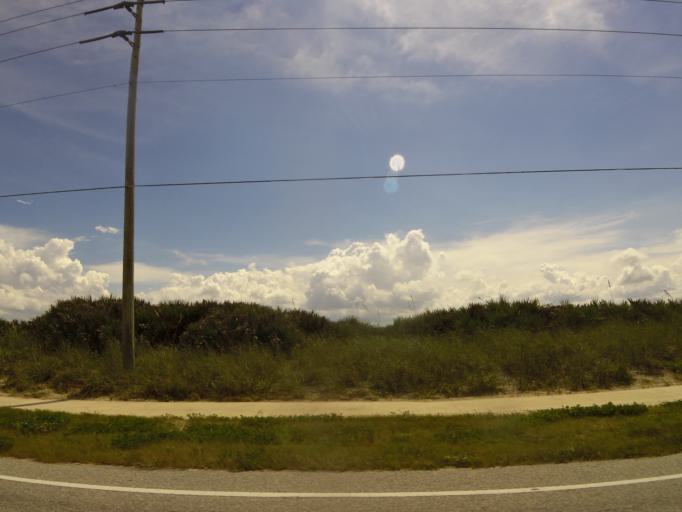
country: US
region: Florida
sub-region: Flagler County
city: Flagler Beach
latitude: 29.4256
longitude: -81.1019
